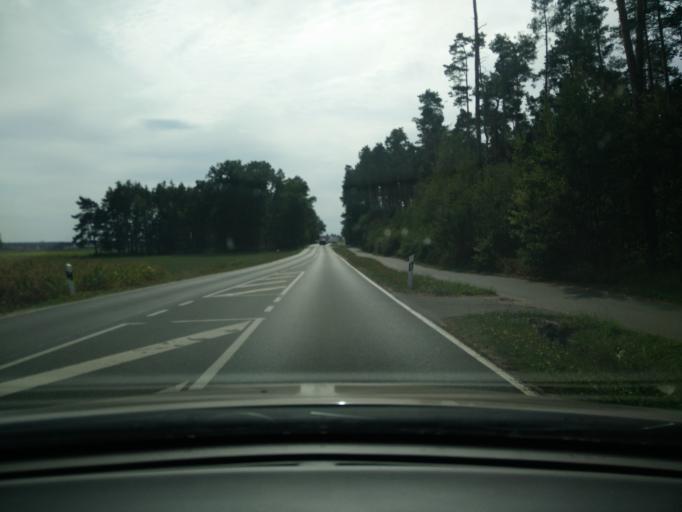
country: DE
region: Bavaria
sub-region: Regierungsbezirk Mittelfranken
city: Veitsbronn
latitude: 49.5006
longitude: 10.8796
